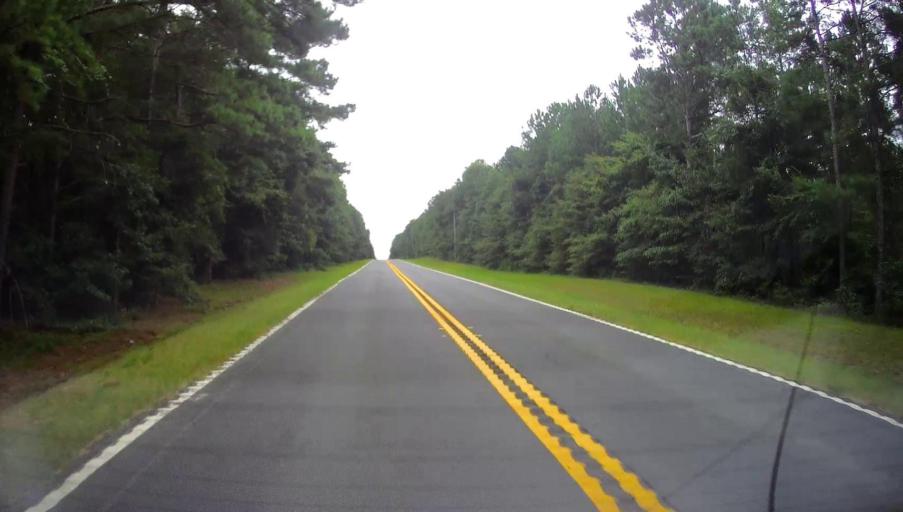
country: US
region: Georgia
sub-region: Dooly County
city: Unadilla
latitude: 32.2911
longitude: -83.8594
